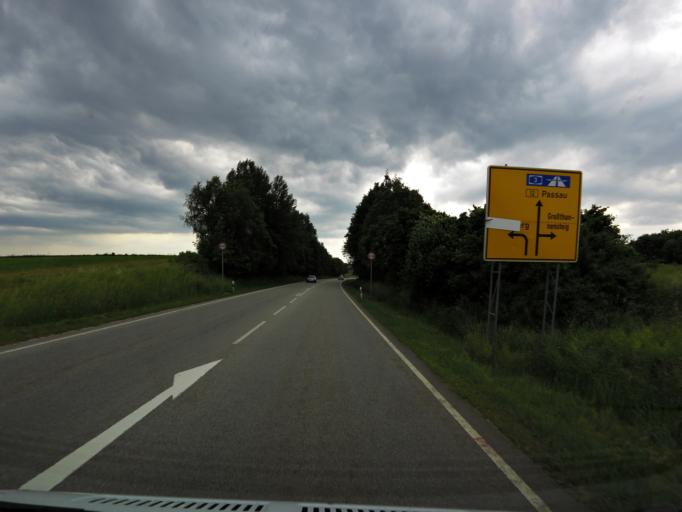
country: DE
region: Bavaria
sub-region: Lower Bavaria
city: Buchlberg
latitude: 48.6941
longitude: 13.5096
